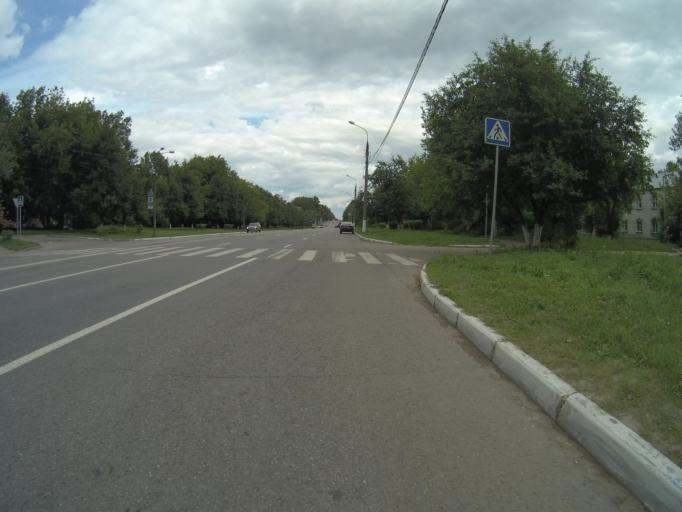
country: RU
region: Vladimir
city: Bogolyubovo
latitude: 56.1691
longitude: 40.4870
